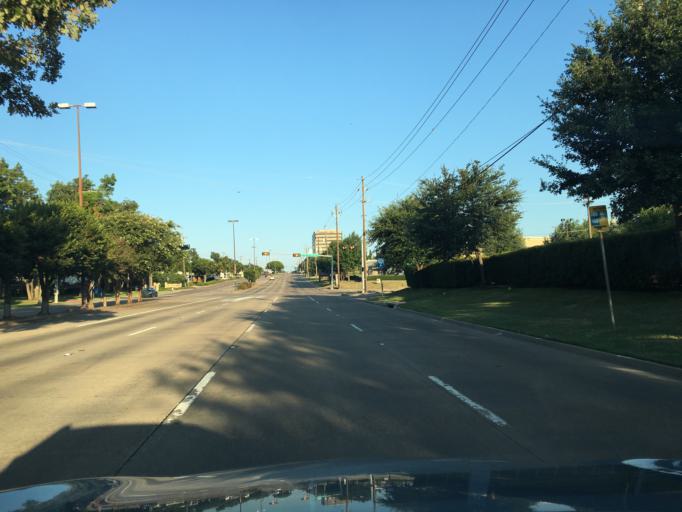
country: US
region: Texas
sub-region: Dallas County
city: Addison
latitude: 32.9541
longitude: -96.8113
